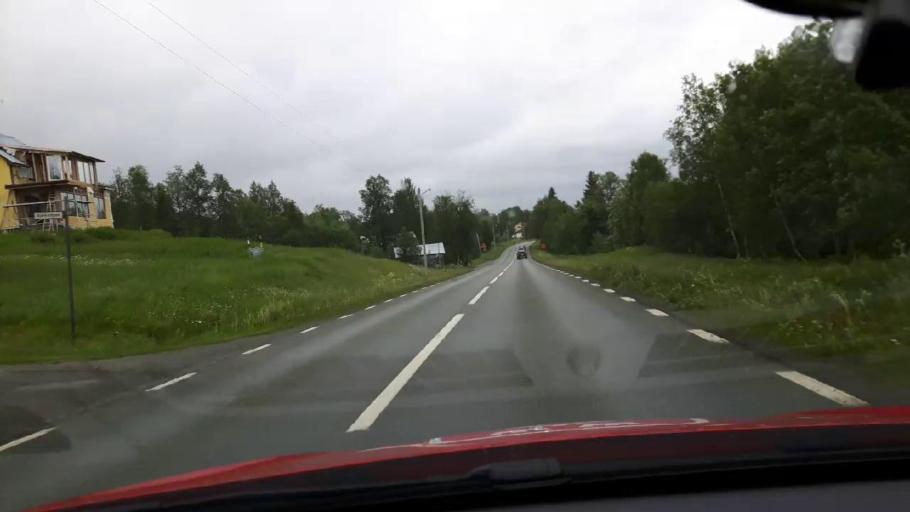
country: SE
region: Jaemtland
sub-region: Are Kommun
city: Are
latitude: 63.3187
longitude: 12.5240
